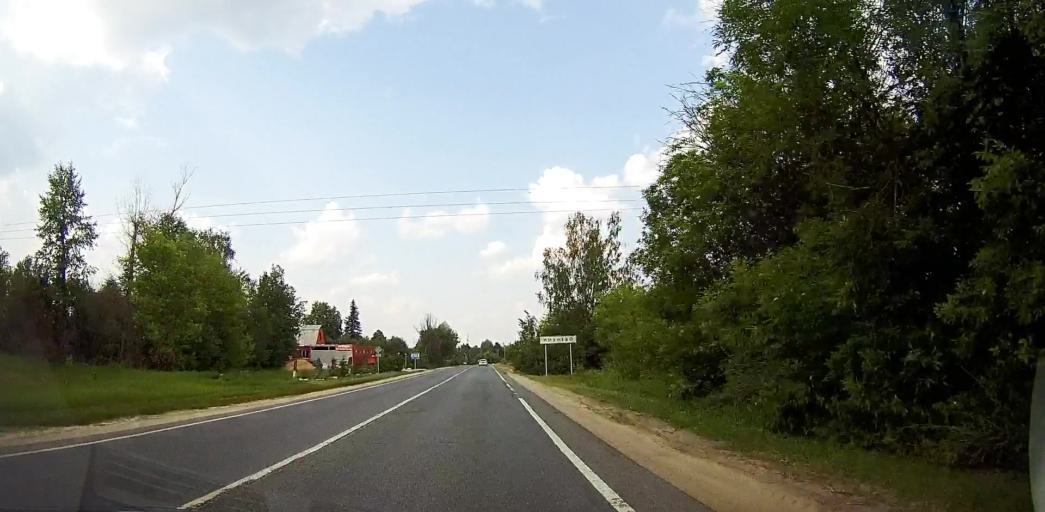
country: RU
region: Moskovskaya
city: Mikhnevo
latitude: 55.1061
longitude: 37.9456
